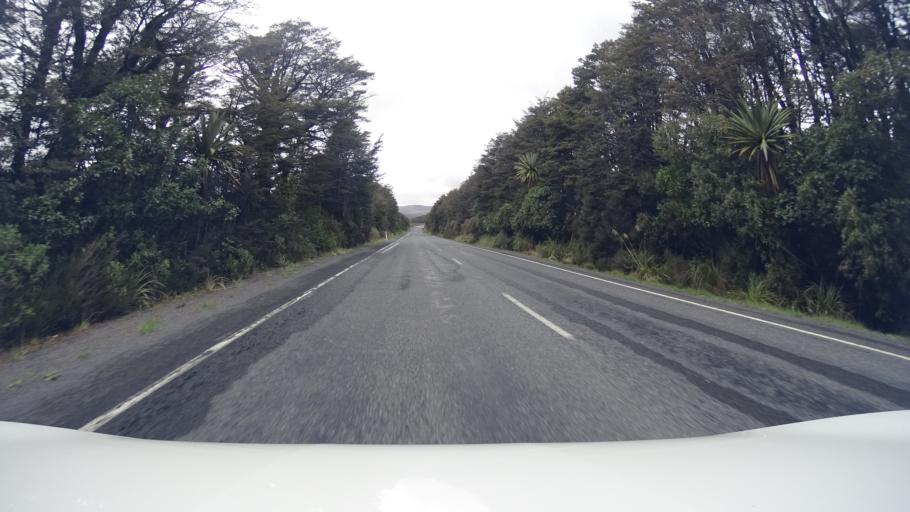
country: NZ
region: Manawatu-Wanganui
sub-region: Ruapehu District
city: Waiouru
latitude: -39.1799
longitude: 175.5203
